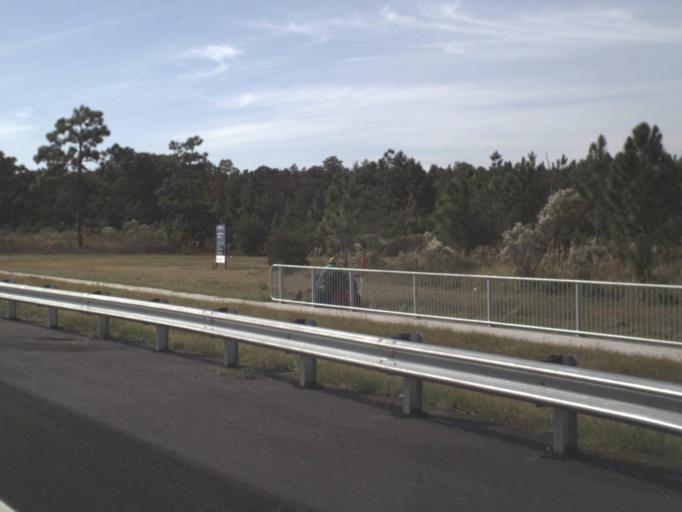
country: US
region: Florida
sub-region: Orange County
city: Williamsburg
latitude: 28.4289
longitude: -81.4231
